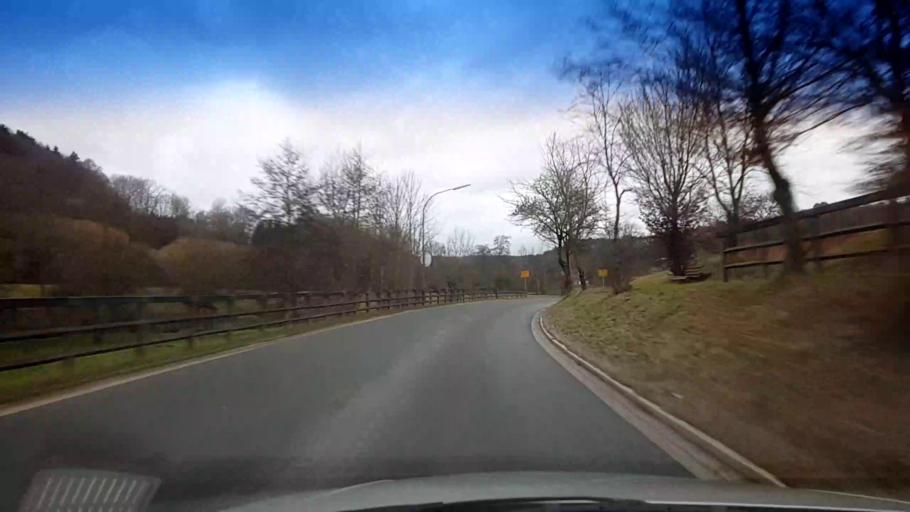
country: DE
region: Bavaria
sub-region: Upper Franconia
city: Wattendorf
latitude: 50.0629
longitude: 11.0717
